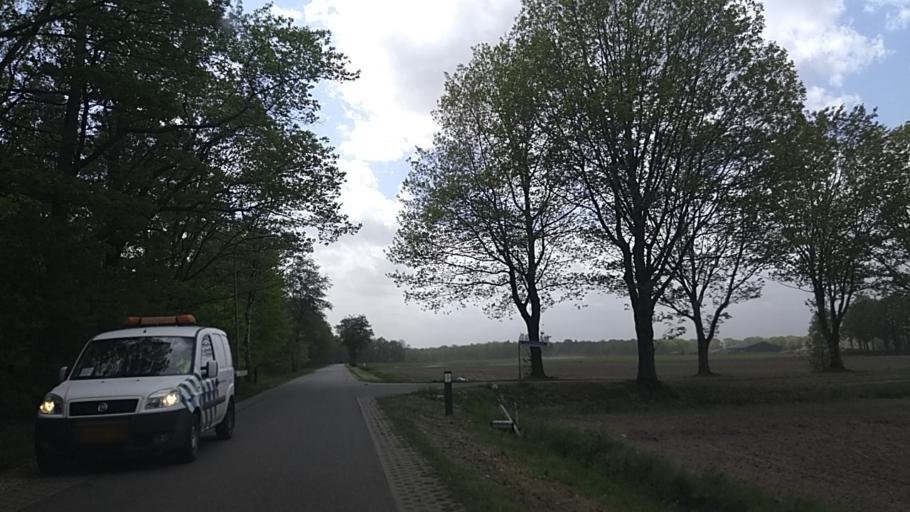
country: NL
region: Limburg
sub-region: Gemeente Leudal
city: Heythuysen
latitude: 51.2990
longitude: 5.8825
